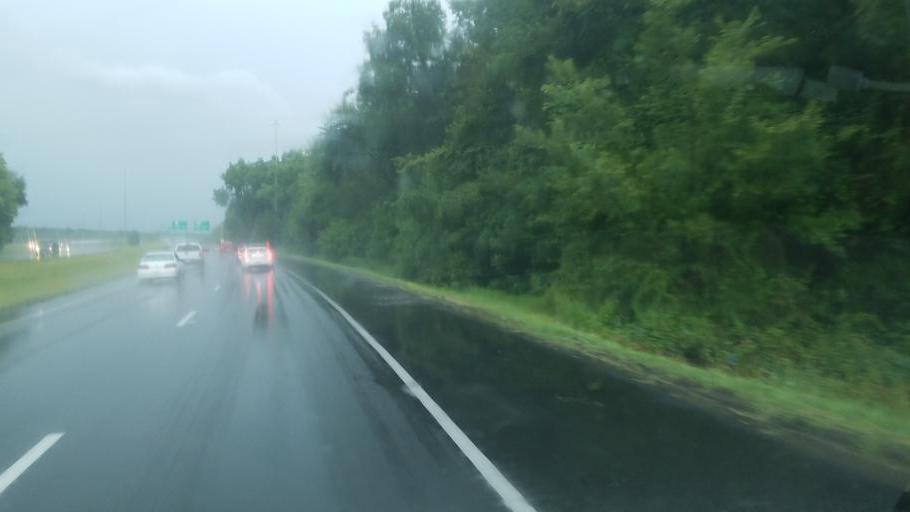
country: US
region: Ohio
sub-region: Trumbull County
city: Howland Center
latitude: 41.2288
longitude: -80.7213
